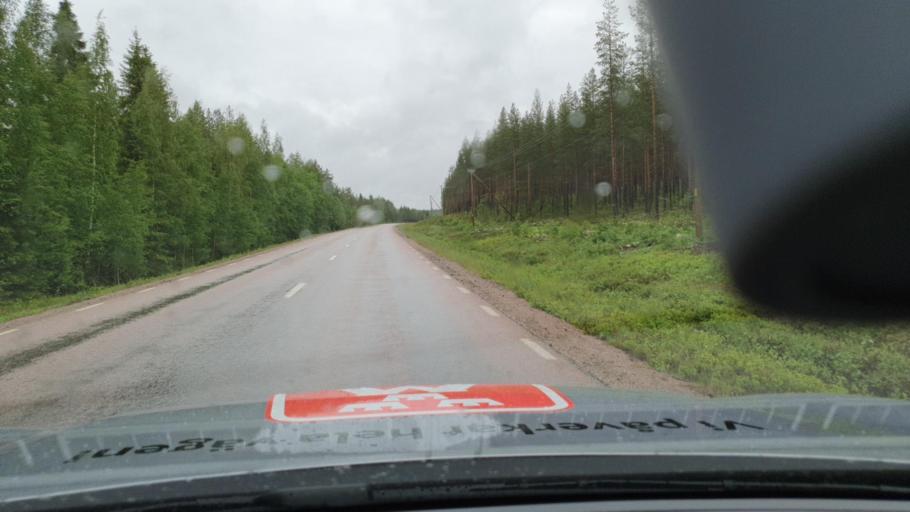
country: SE
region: Norrbotten
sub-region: Overkalix Kommun
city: OEverkalix
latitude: 66.4029
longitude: 22.9537
